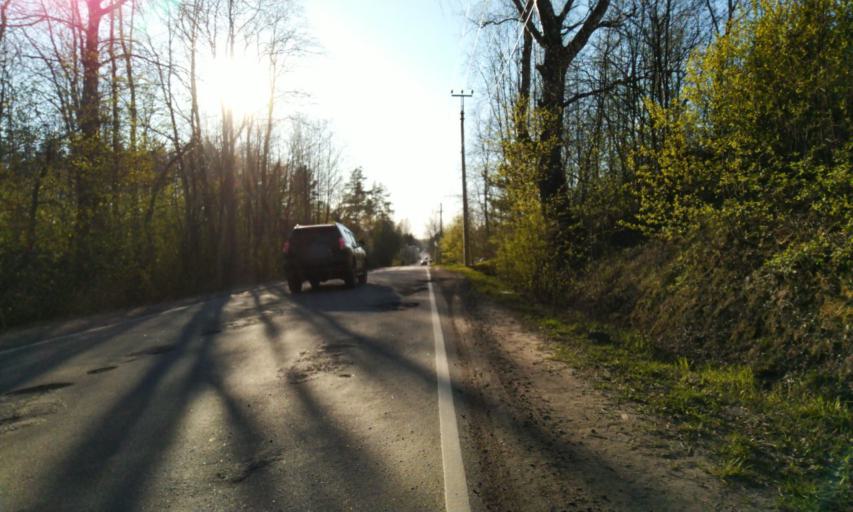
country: RU
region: Leningrad
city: Toksovo
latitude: 60.1414
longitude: 30.5367
